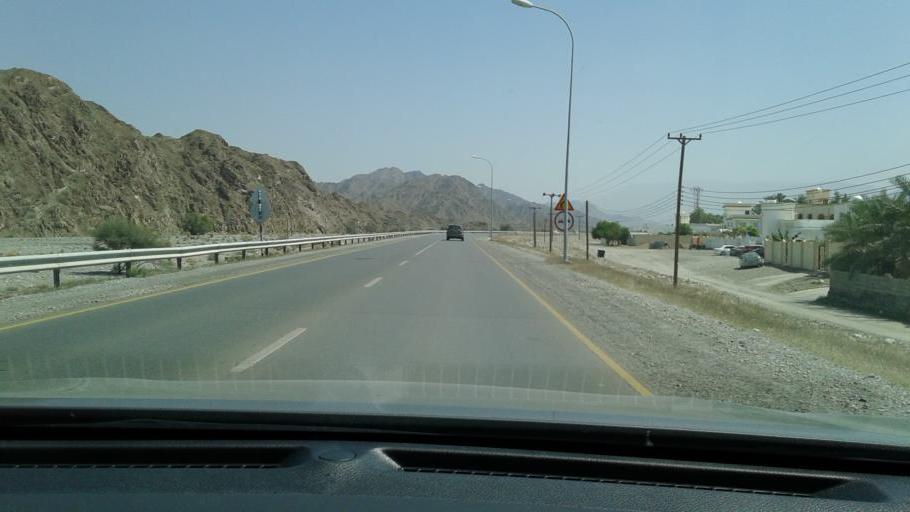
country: OM
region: Al Batinah
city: Rustaq
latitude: 23.3994
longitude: 57.4326
